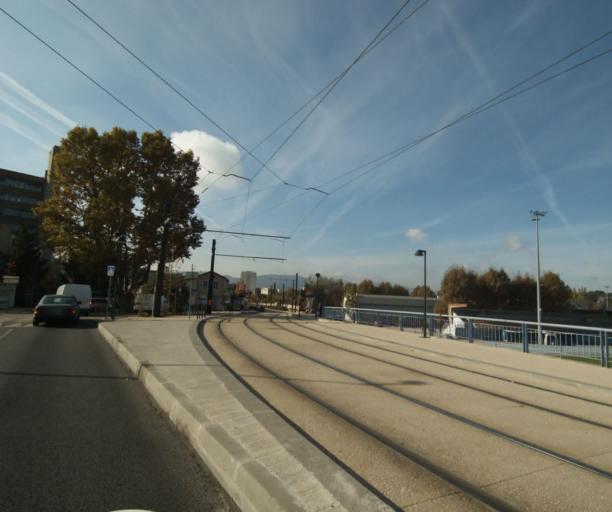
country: FR
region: Provence-Alpes-Cote d'Azur
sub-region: Departement des Bouches-du-Rhone
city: Aubagne
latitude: 43.2933
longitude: 5.5633
